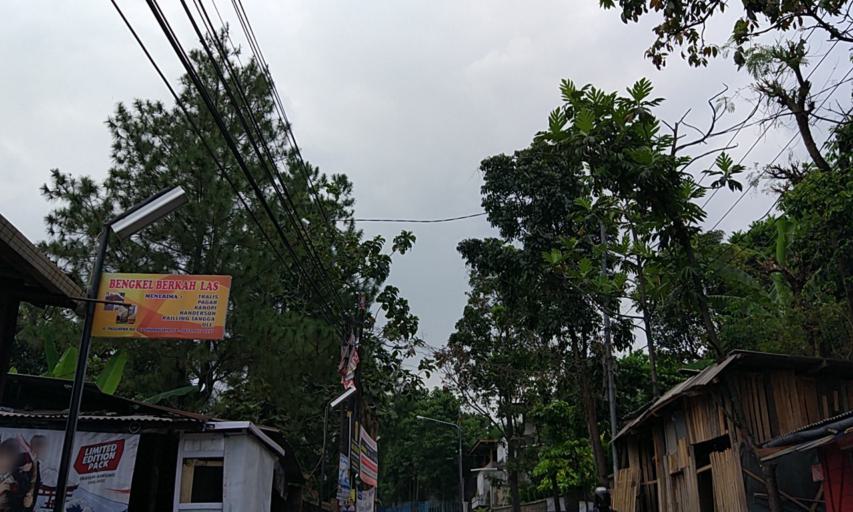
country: ID
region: West Java
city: Bandung
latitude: -6.8975
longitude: 107.6818
